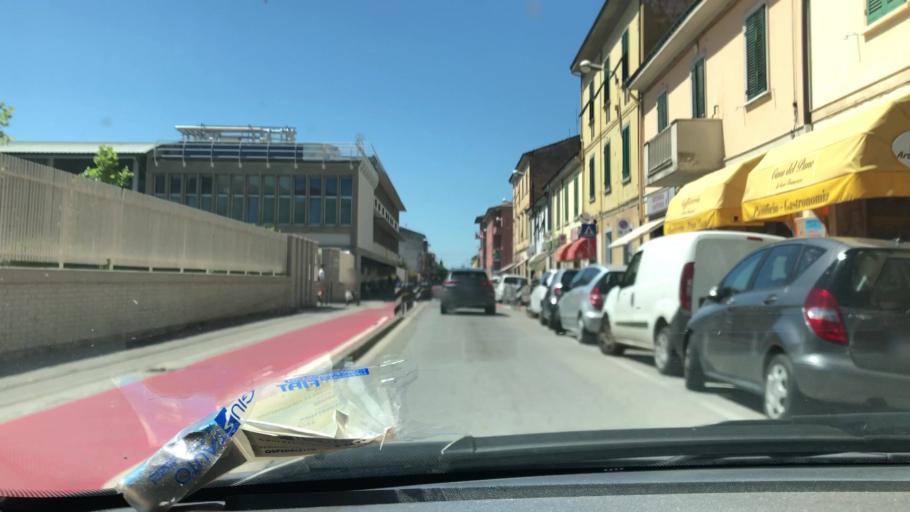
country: IT
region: Tuscany
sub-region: Province of Pisa
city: Pontedera
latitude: 43.6599
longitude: 10.6335
